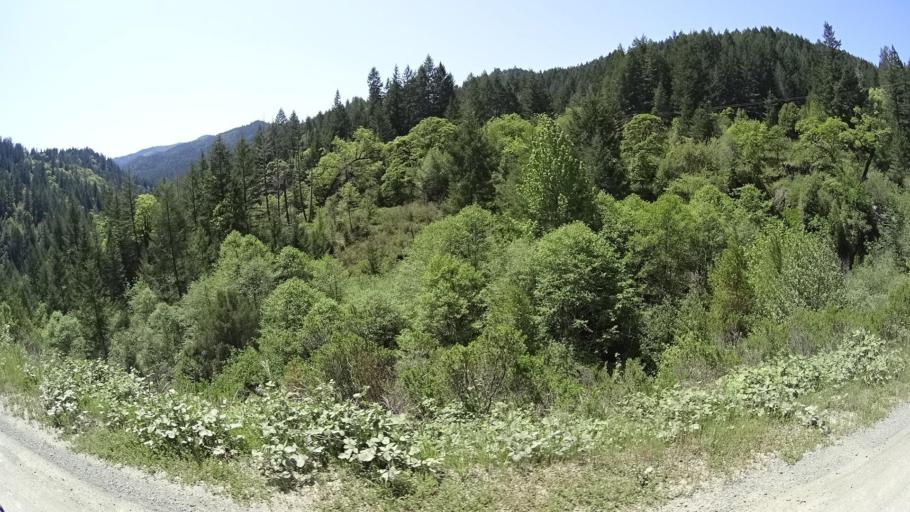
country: US
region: California
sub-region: Humboldt County
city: Redway
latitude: 40.2030
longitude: -123.5229
